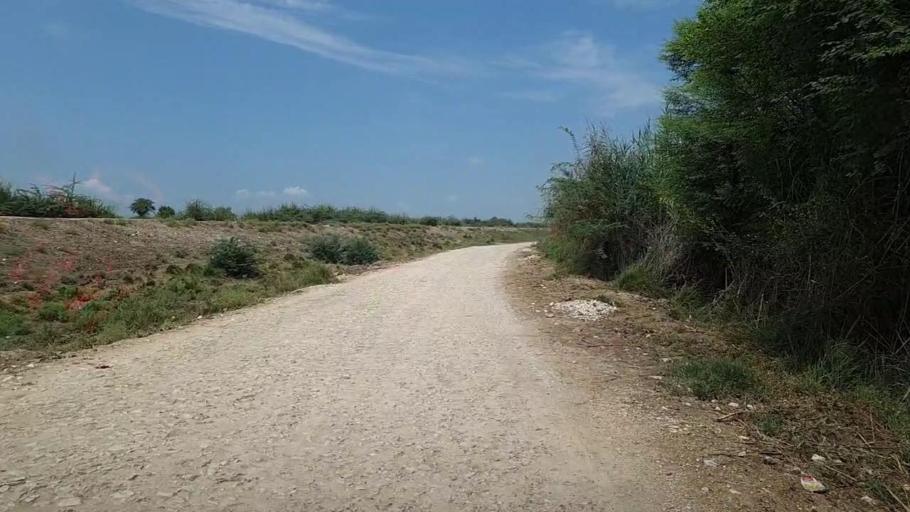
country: PK
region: Sindh
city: Bhiria
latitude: 26.9070
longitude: 68.2018
